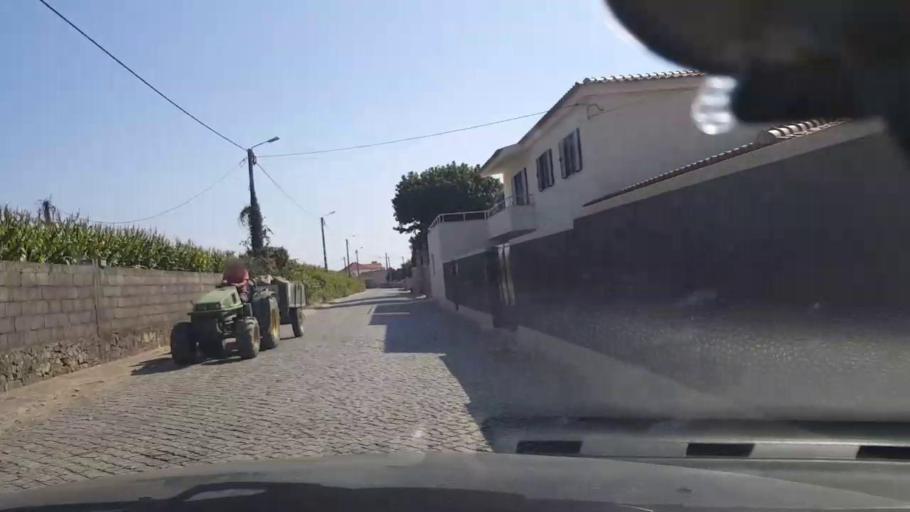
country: PT
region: Porto
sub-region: Povoa de Varzim
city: Pedroso
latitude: 41.4089
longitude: -8.6935
